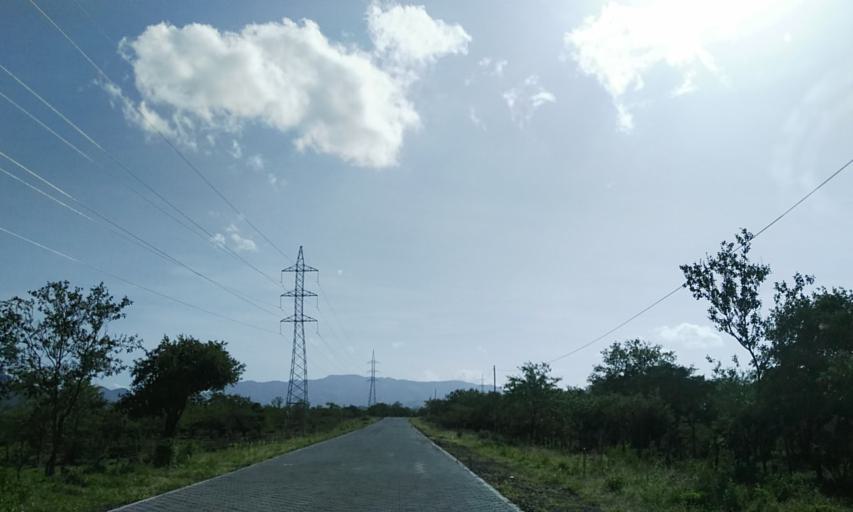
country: NI
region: Matagalpa
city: Ciudad Dario
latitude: 12.7282
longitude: -86.0833
